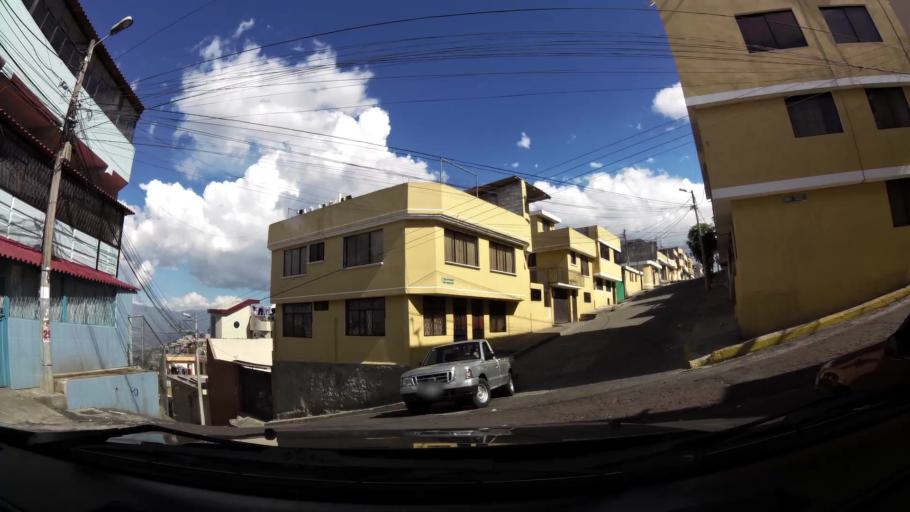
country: EC
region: Pichincha
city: Quito
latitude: -0.1206
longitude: -78.4641
